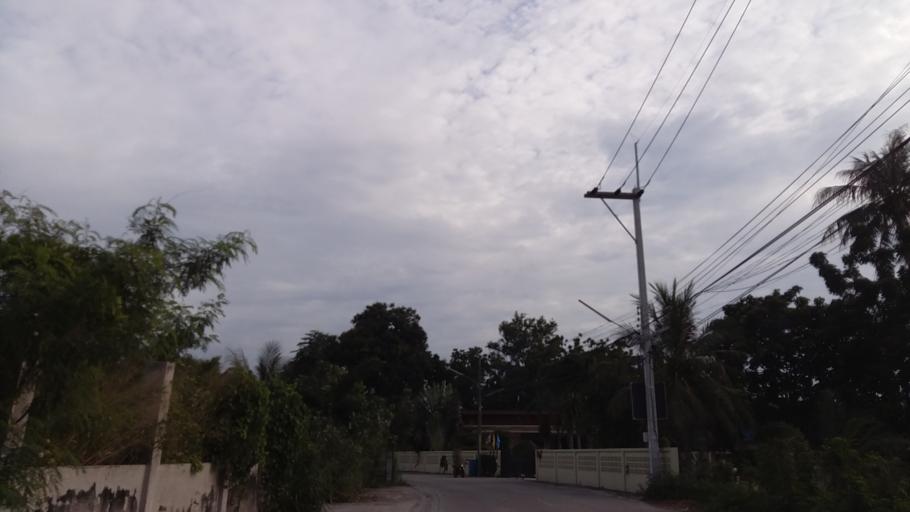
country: TH
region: Chon Buri
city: Chon Buri
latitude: 13.3067
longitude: 100.9388
